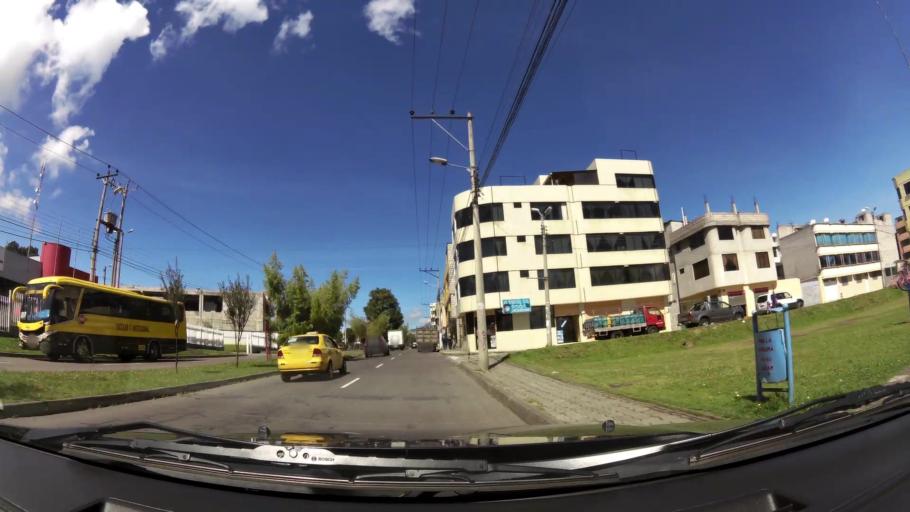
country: EC
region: Pichincha
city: Quito
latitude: -0.2904
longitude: -78.5428
